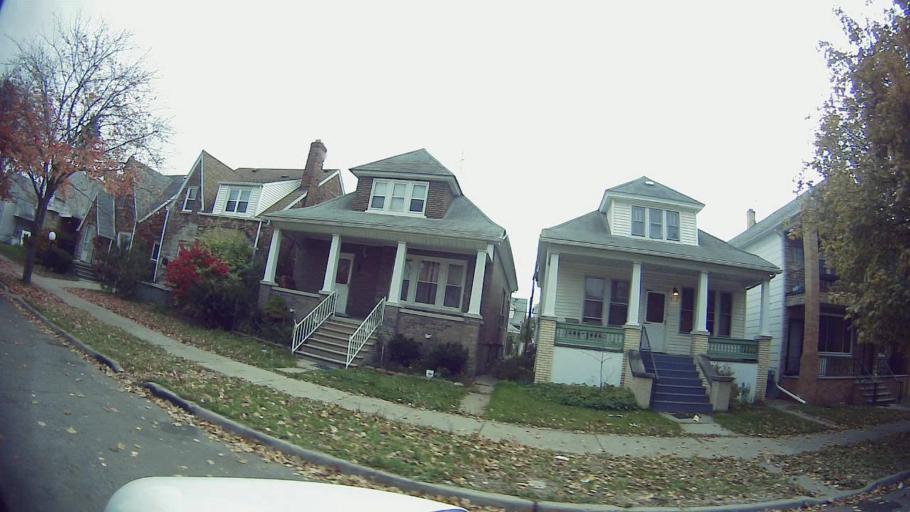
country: US
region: Michigan
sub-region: Wayne County
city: Hamtramck
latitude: 42.4032
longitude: -83.0506
